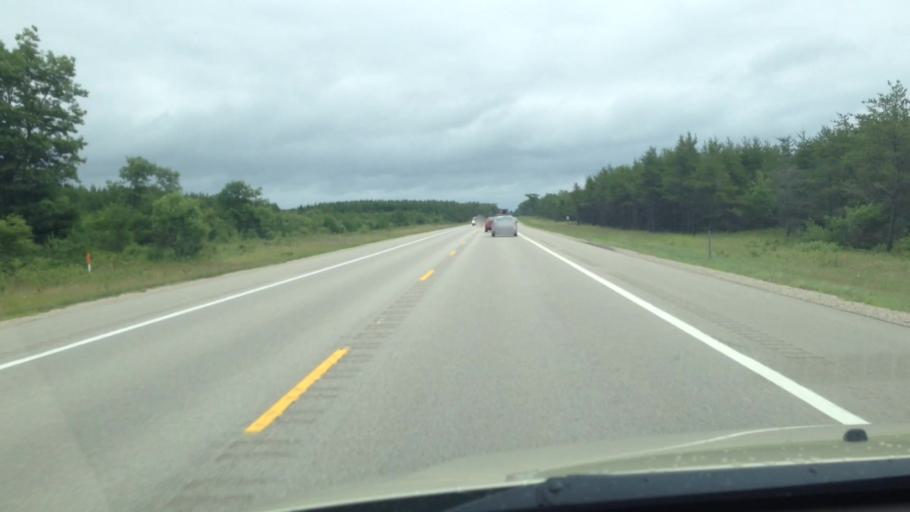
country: US
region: Michigan
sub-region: Schoolcraft County
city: Manistique
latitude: 45.9056
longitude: -86.3962
